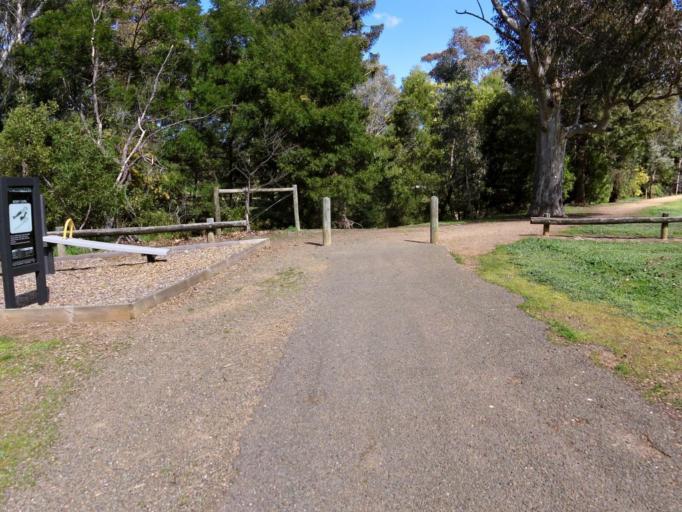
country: AU
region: Victoria
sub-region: Murrindindi
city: Alexandra
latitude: -37.1876
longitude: 145.7144
